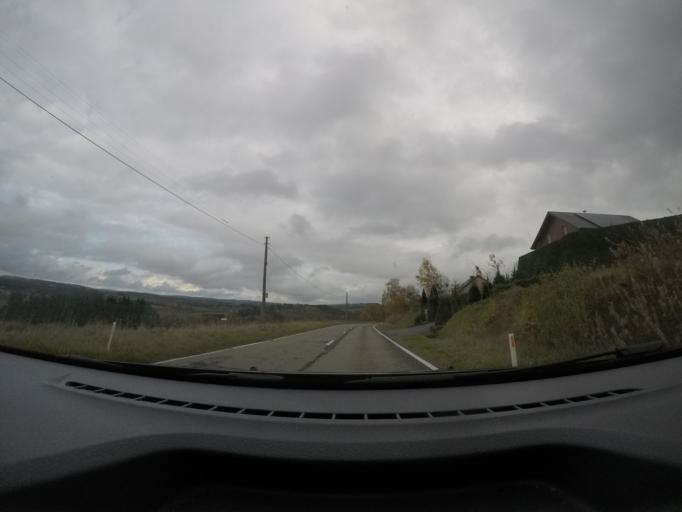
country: BE
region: Wallonia
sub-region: Province du Luxembourg
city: Houffalize
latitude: 50.1479
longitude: 5.7133
